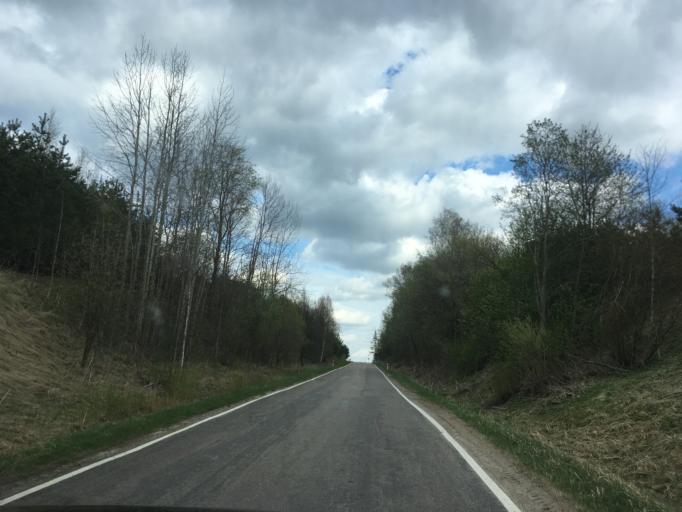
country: PL
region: Podlasie
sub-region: Powiat suwalski
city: Filipow
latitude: 54.3589
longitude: 22.8139
